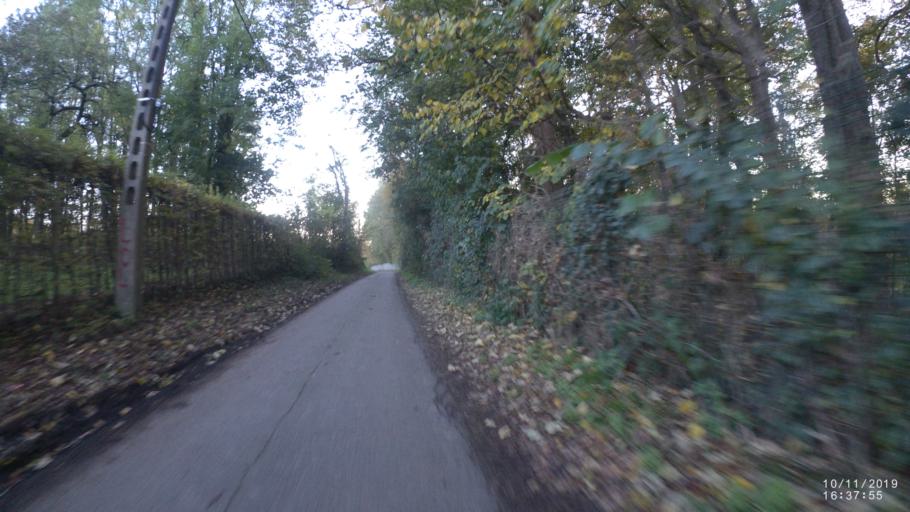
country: BE
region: Flanders
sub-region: Provincie Vlaams-Brabant
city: Bierbeek
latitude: 50.8659
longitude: 4.7754
